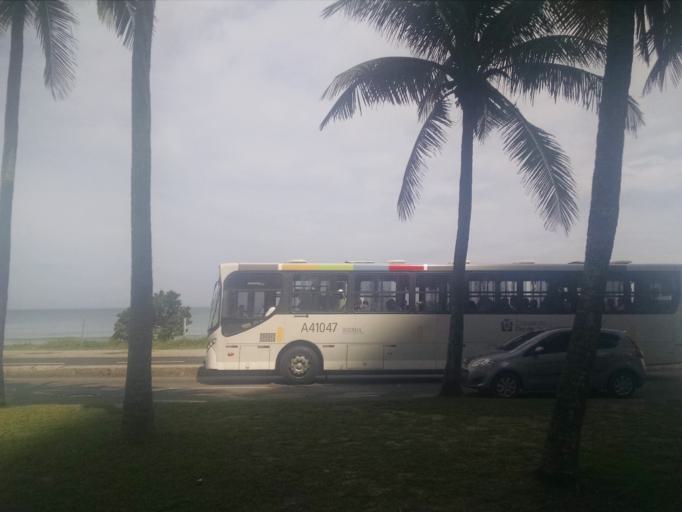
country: BR
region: Rio de Janeiro
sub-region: Rio De Janeiro
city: Rio de Janeiro
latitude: -23.0111
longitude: -43.3284
